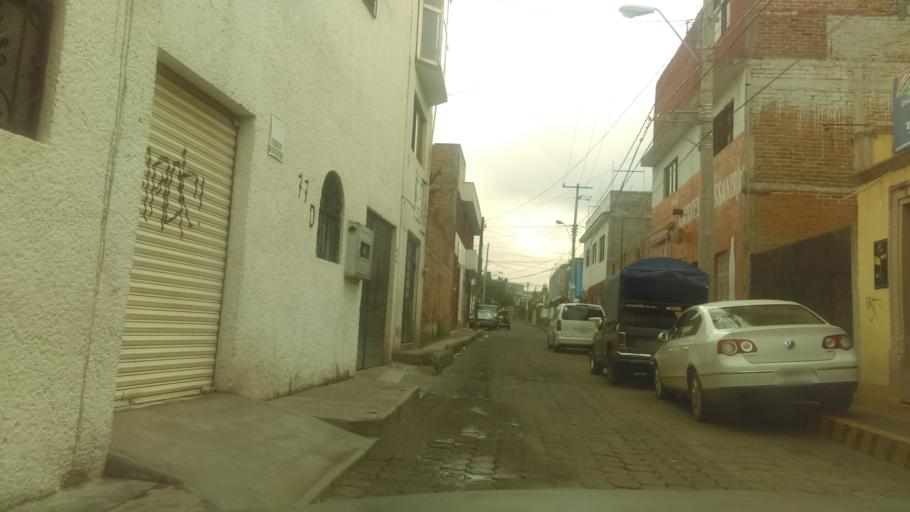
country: MX
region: Michoacan
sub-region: Morelia
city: Montana Monarca (Punta Altozano)
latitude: 19.6722
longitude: -101.1897
